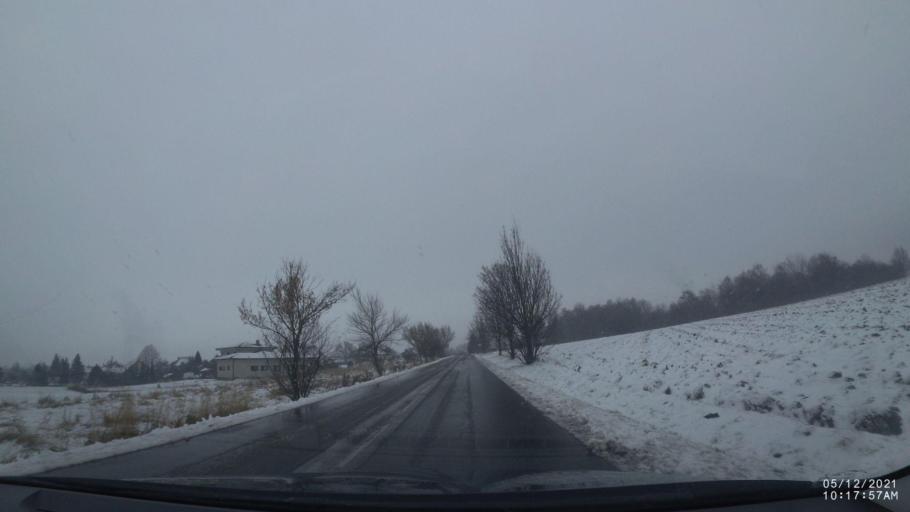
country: CZ
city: Vamberk
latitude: 50.1089
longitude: 16.2911
